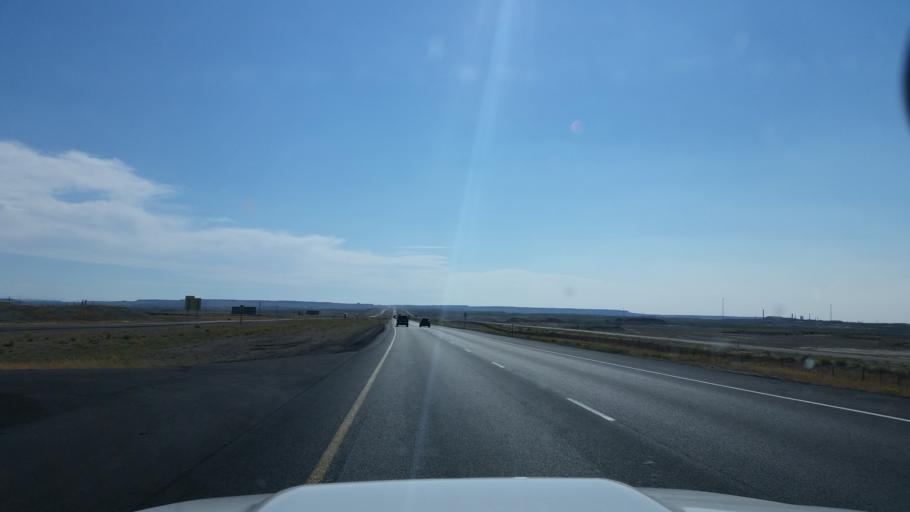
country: US
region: Wyoming
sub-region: Uinta County
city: Lyman
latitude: 41.5413
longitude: -109.9222
